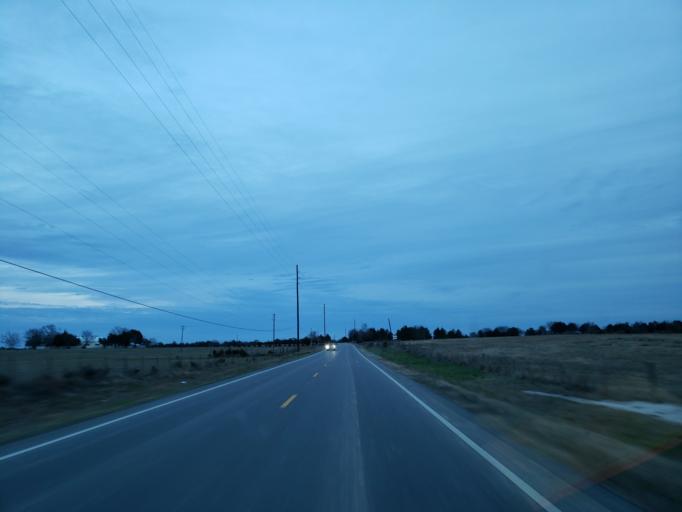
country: US
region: Alabama
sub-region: Sumter County
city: Livingston
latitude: 32.8121
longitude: -88.2752
